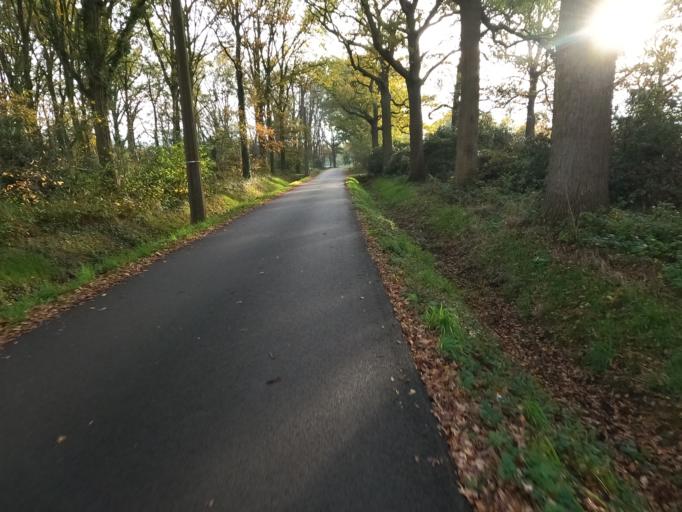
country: BE
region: Flanders
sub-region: Provincie Antwerpen
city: Berlaar
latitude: 51.1360
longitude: 4.6486
